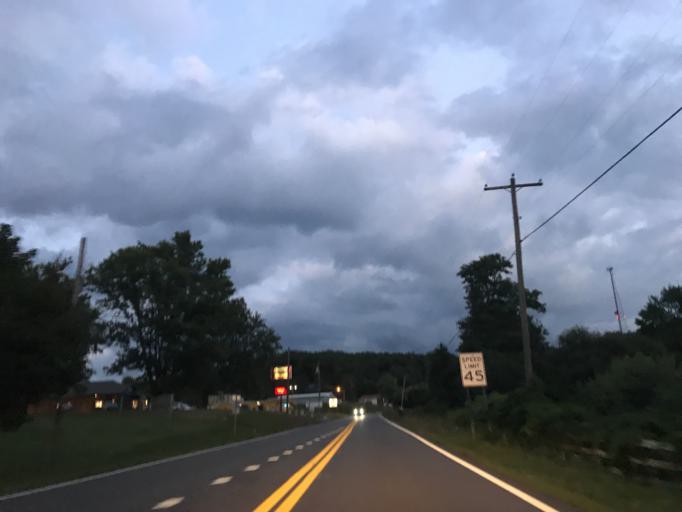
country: US
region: West Virginia
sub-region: Hancock County
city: Chester
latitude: 40.5980
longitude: -80.5323
